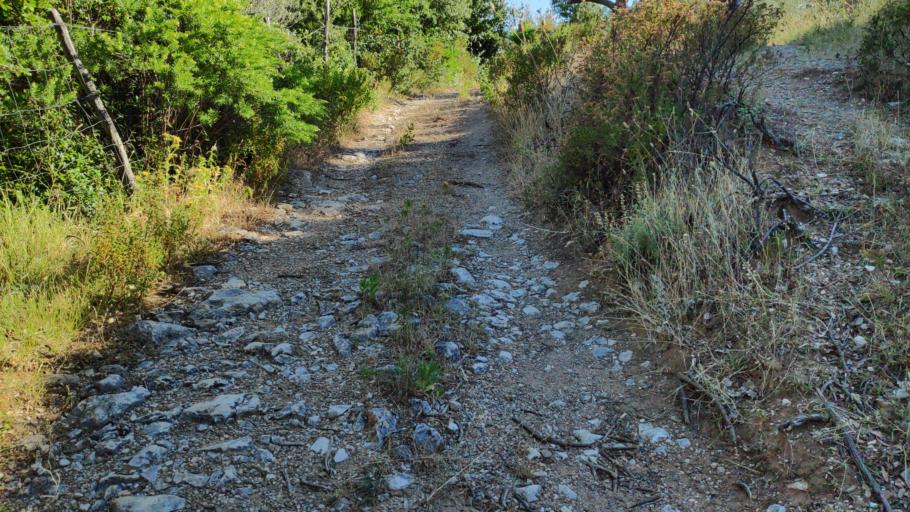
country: IT
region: Calabria
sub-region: Provincia di Reggio Calabria
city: Pazzano
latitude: 38.4556
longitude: 16.4358
